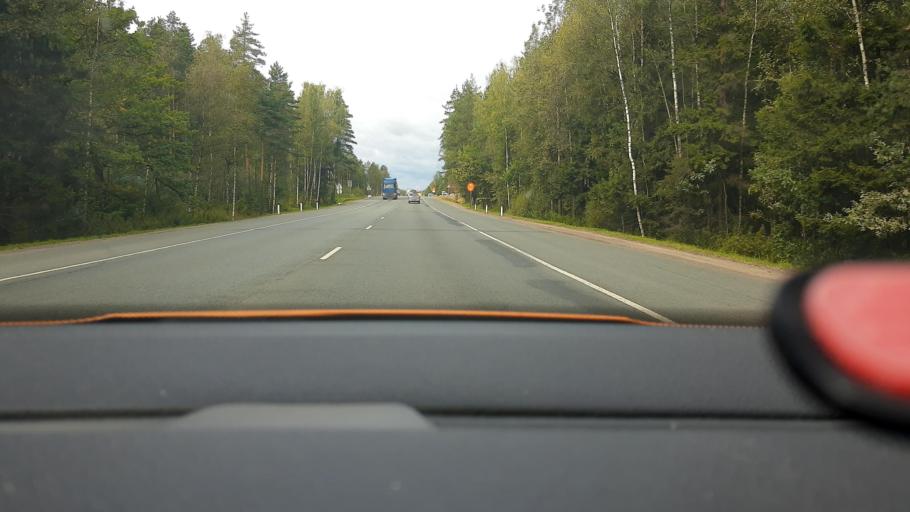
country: RU
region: Moskovskaya
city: Zelenogradskiy
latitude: 56.1009
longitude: 37.9703
